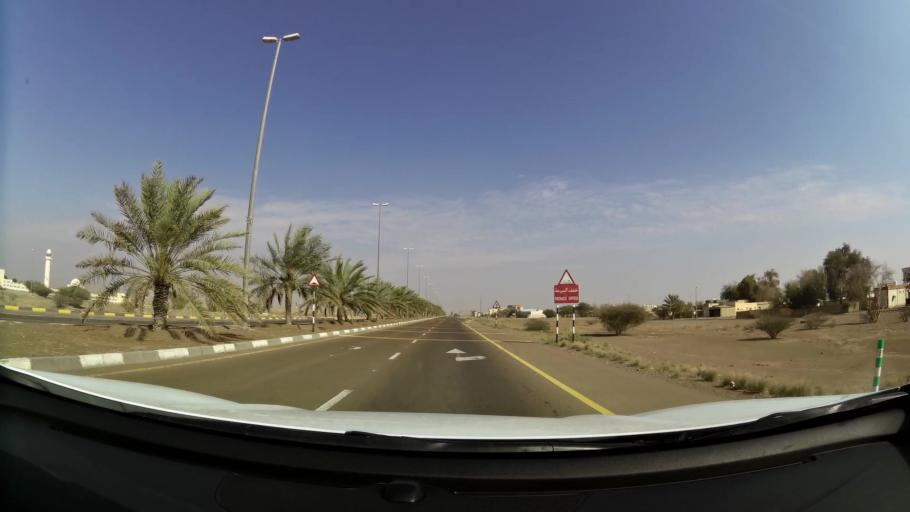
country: AE
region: Abu Dhabi
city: Al Ain
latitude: 24.0940
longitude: 55.9259
